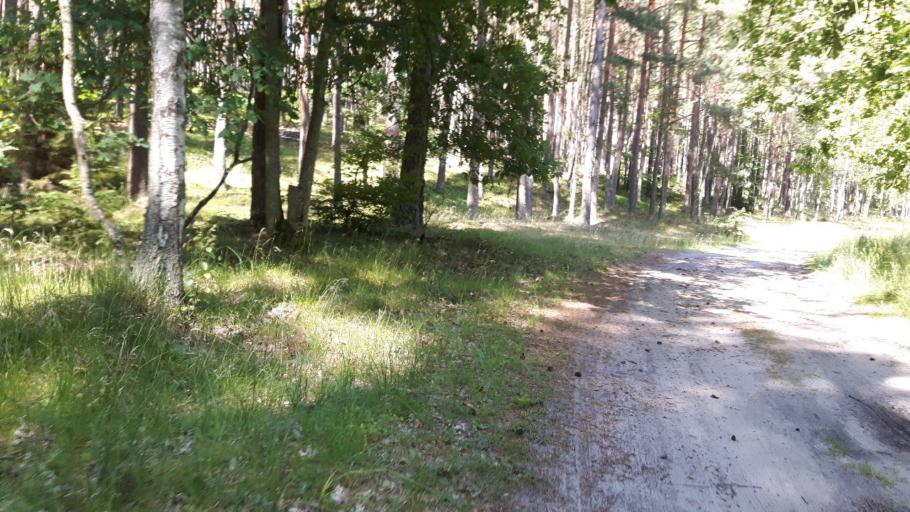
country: PL
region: Pomeranian Voivodeship
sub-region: Powiat leborski
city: Leba
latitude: 54.6988
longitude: 17.4859
